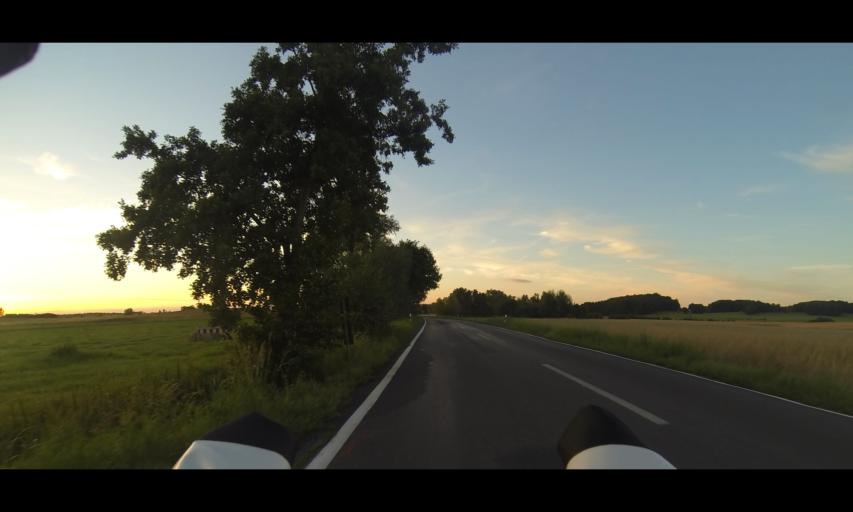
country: DE
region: Saxony
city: Moritzburg
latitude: 51.1529
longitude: 13.7325
